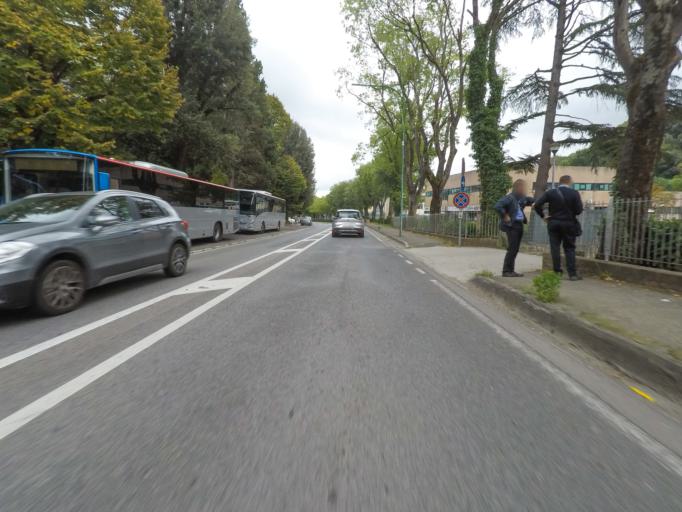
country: IT
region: Tuscany
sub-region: Provincia di Siena
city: Siena
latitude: 43.3246
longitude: 11.3441
